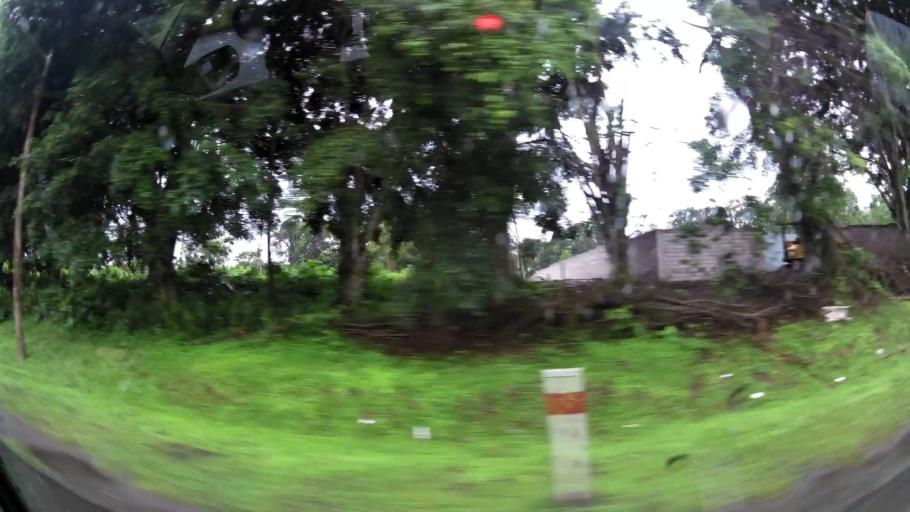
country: EC
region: Santo Domingo de los Tsachilas
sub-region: Canton Santo Domingo de los Colorados
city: Santo Domingo de los Colorados
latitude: -0.2348
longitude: -79.1568
